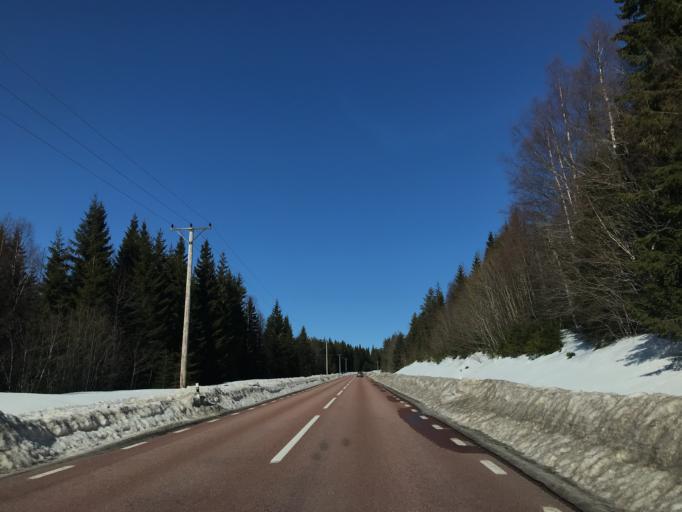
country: SE
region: Dalarna
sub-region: Vansbro Kommun
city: Vansbro
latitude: 60.2749
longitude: 14.1701
